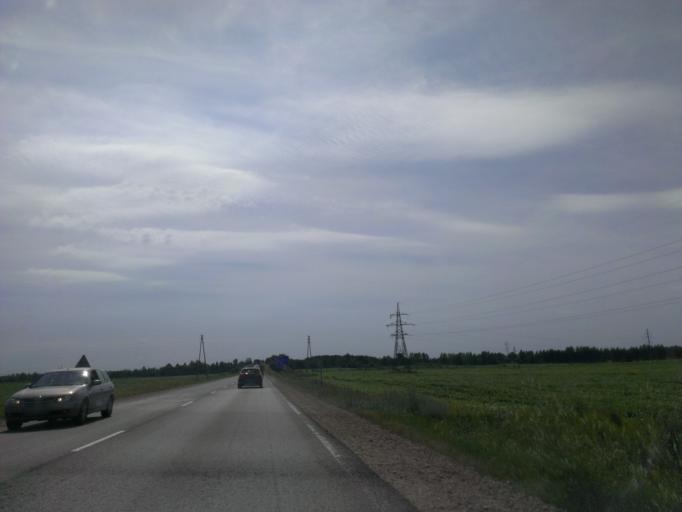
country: LV
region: Salaspils
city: Salaspils
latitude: 56.8592
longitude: 24.4036
